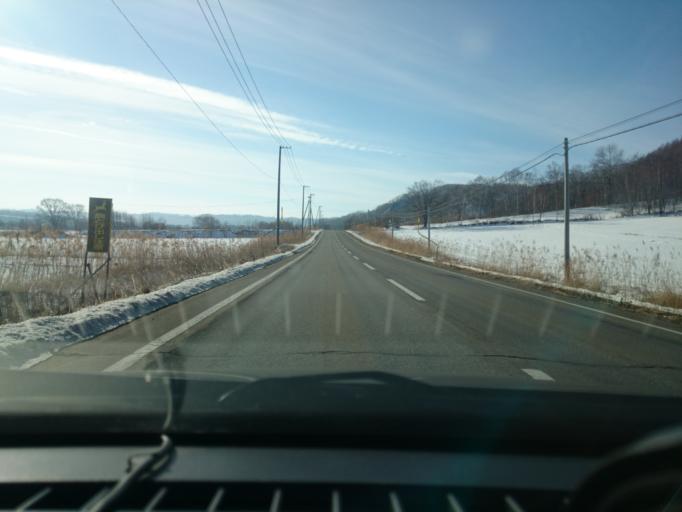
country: JP
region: Hokkaido
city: Otofuke
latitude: 43.2603
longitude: 143.5748
